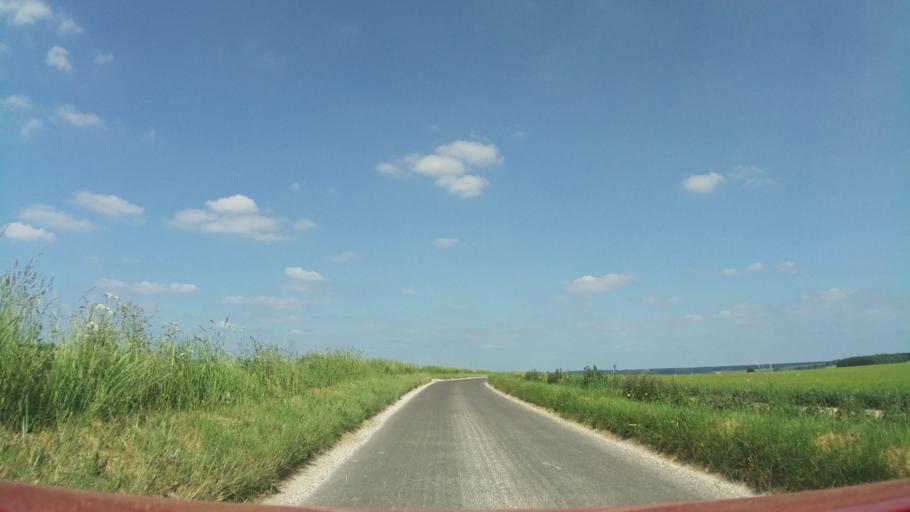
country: GB
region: England
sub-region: Wiltshire
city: Collingbourne Kingston
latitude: 51.2814
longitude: -1.6939
